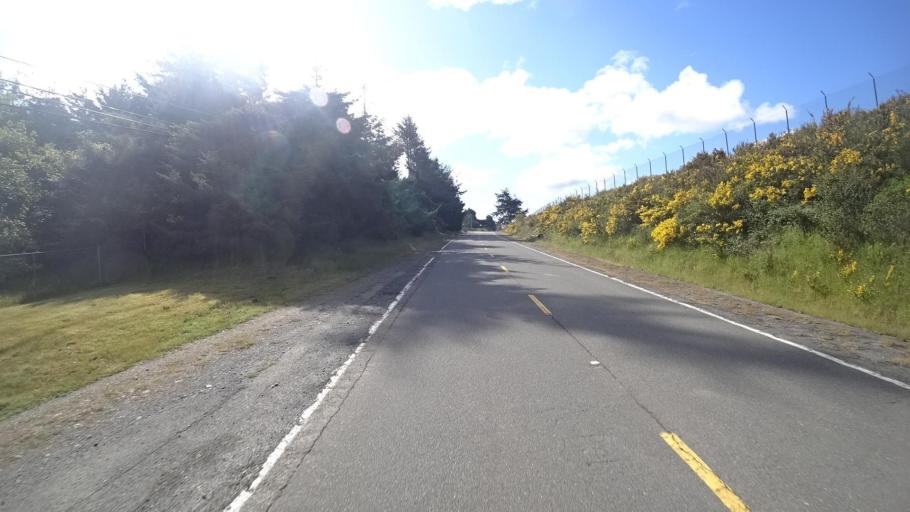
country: US
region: California
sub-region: Humboldt County
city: McKinleyville
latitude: 40.9835
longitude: -124.1035
